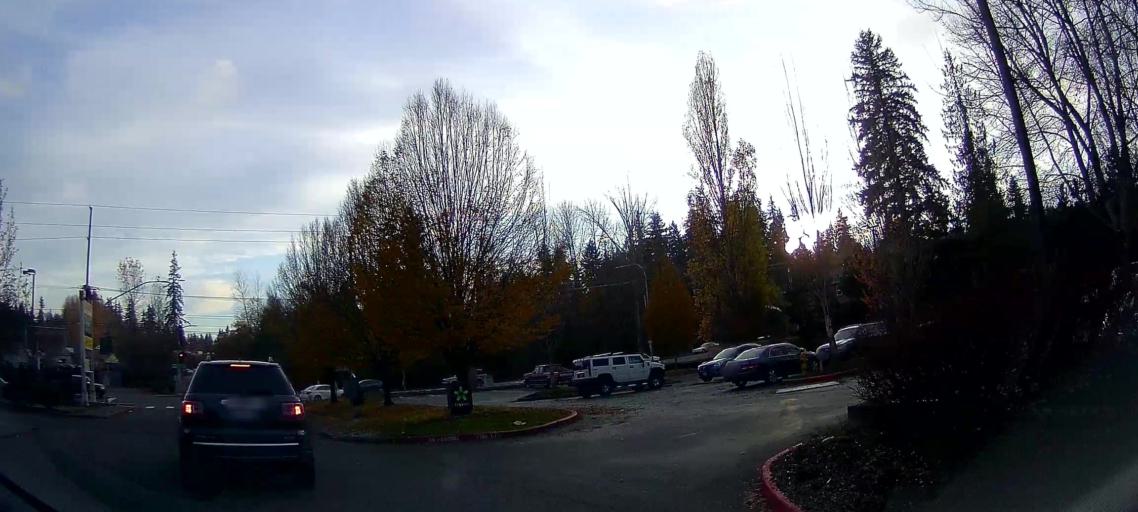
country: US
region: Washington
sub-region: King County
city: Bothell
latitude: 47.7920
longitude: -122.2189
